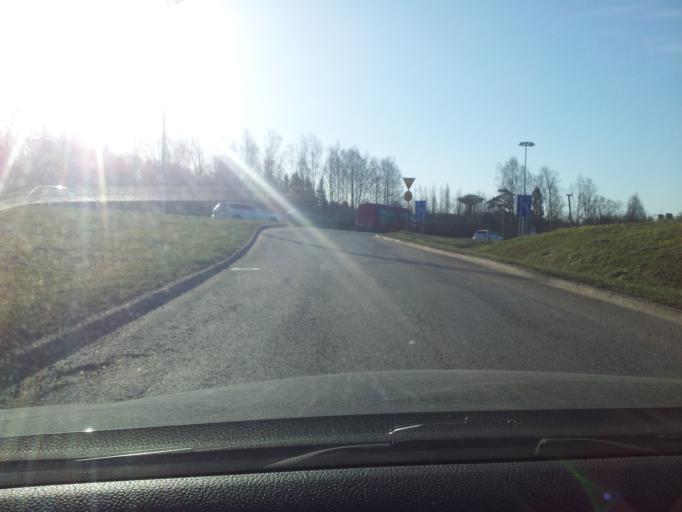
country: FI
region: Uusimaa
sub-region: Helsinki
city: Koukkuniemi
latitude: 60.1677
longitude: 24.7514
